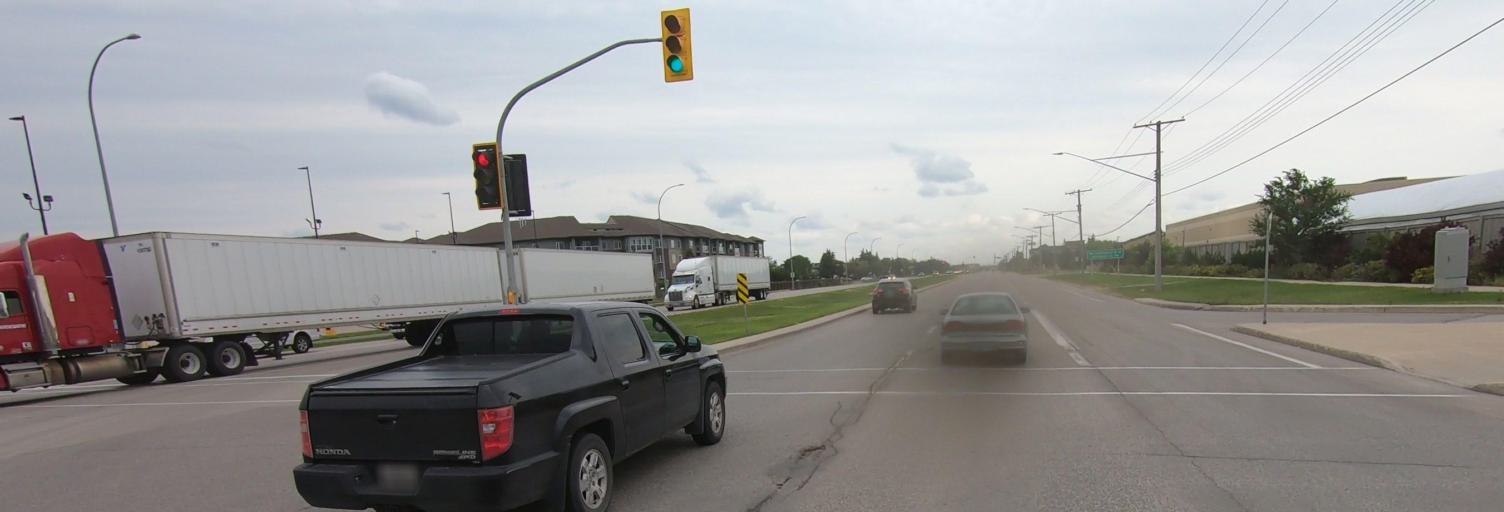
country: CA
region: Manitoba
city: Winnipeg
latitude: 49.8221
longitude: -97.1983
